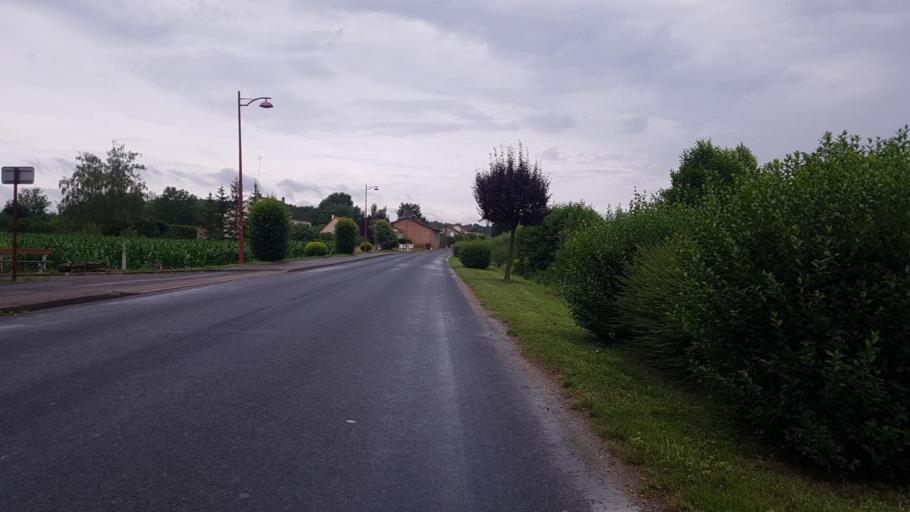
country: FR
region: Champagne-Ardenne
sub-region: Departement de la Marne
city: Vitry-le-Francois
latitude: 48.7421
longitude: 4.6332
